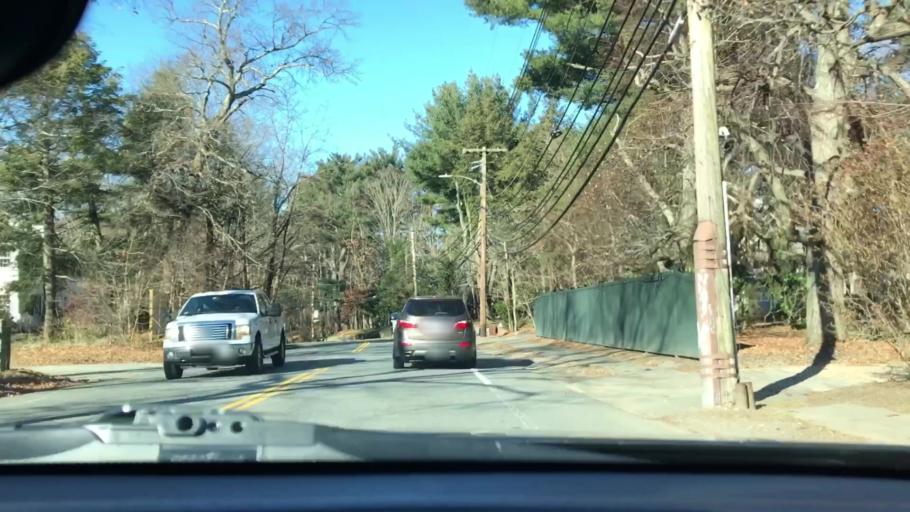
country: US
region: Massachusetts
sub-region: Norfolk County
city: Dedham
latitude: 42.2524
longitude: -71.1847
